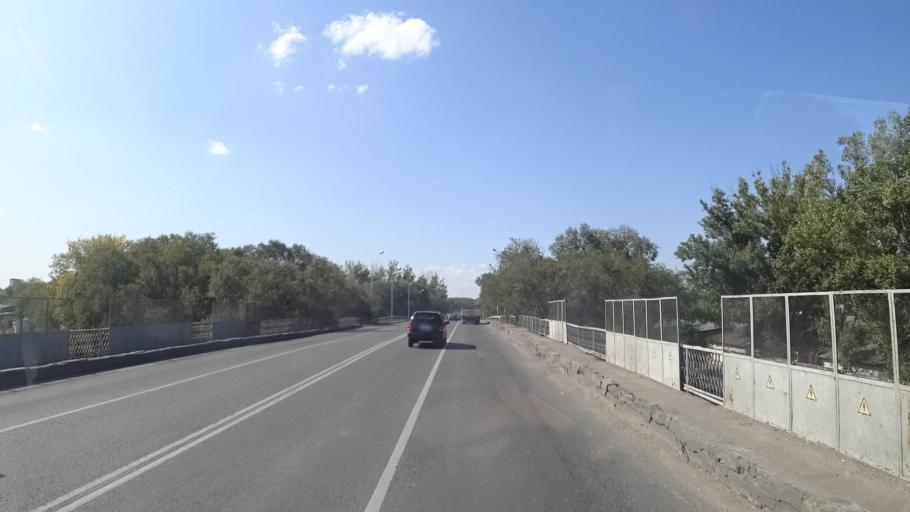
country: KZ
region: Almaty Oblysy
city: Pervomayskiy
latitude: 43.3424
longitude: 76.9782
